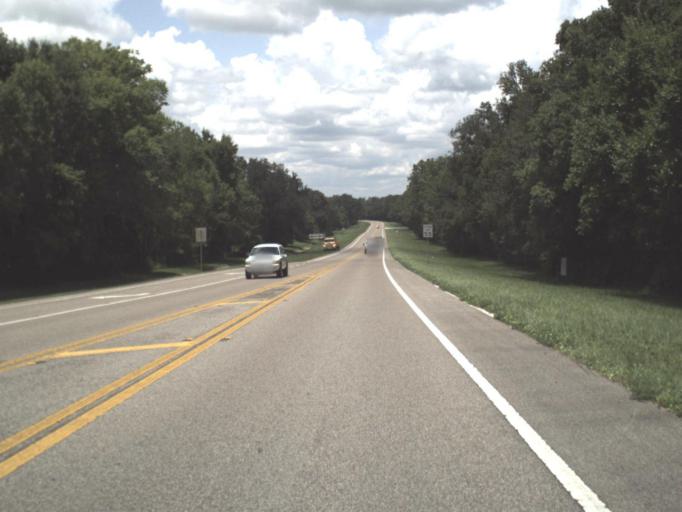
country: US
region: Florida
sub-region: Hernando County
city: North Brooksville
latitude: 28.5966
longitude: -82.4007
